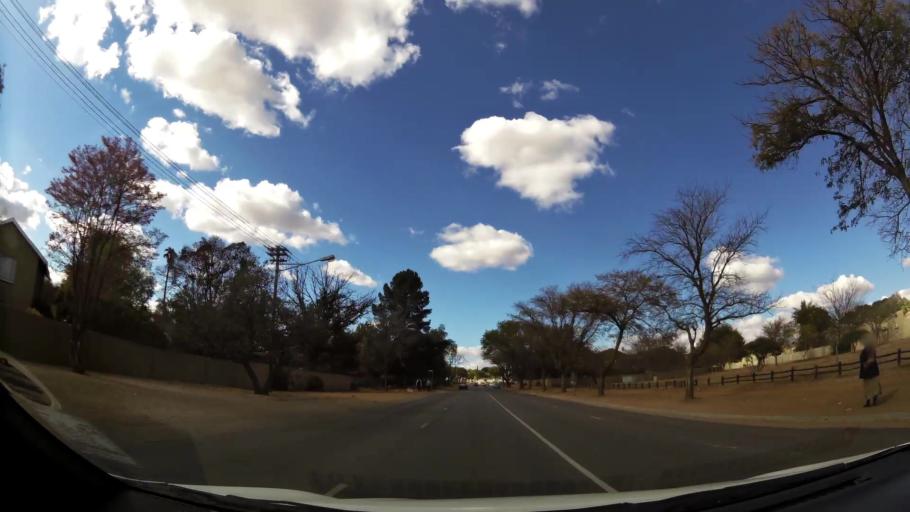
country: ZA
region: Limpopo
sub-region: Capricorn District Municipality
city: Polokwane
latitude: -23.8935
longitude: 29.4701
